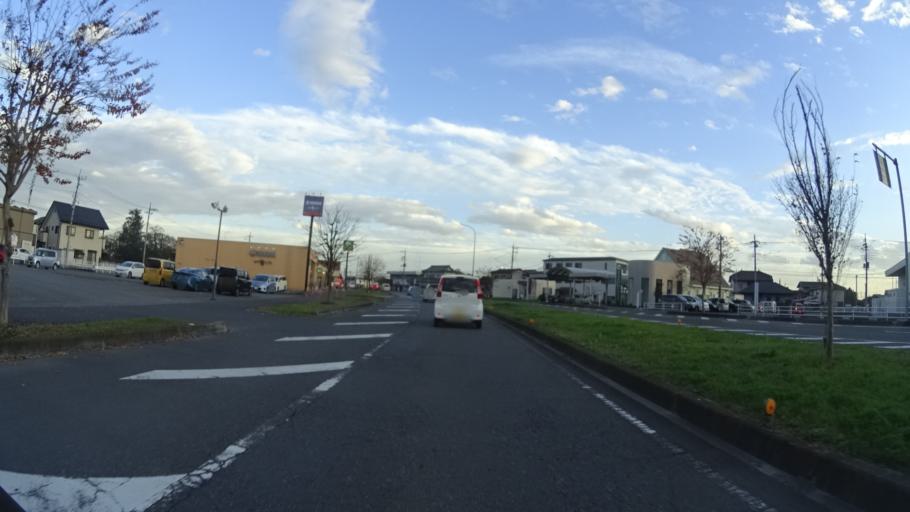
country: JP
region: Tochigi
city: Tochigi
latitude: 36.3926
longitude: 139.7259
